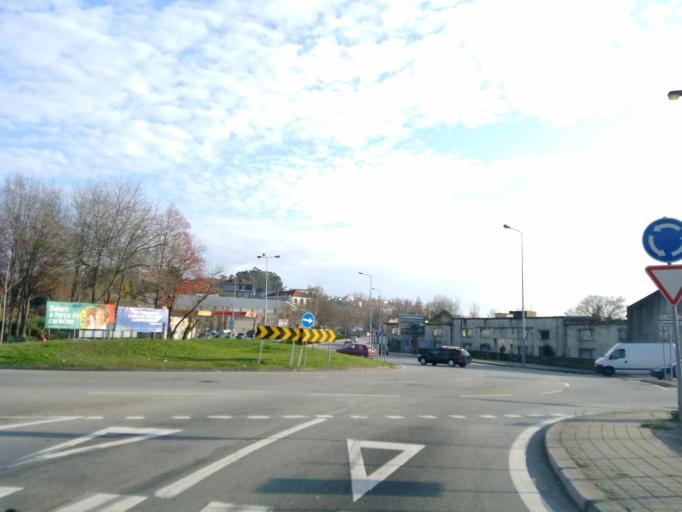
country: PT
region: Porto
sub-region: Gondomar
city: Valbom
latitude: 41.1463
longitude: -8.5796
